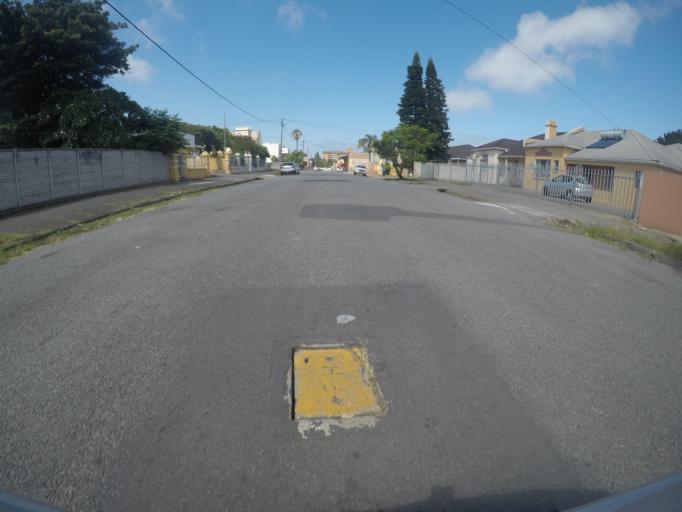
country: ZA
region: Eastern Cape
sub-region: Buffalo City Metropolitan Municipality
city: East London
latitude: -33.0043
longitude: 27.8977
